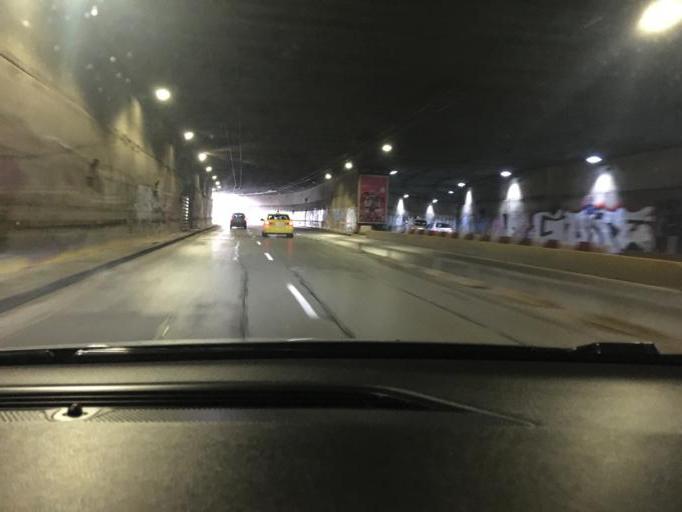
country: BG
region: Sofia-Capital
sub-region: Stolichna Obshtina
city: Sofia
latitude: 42.6861
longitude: 23.3197
